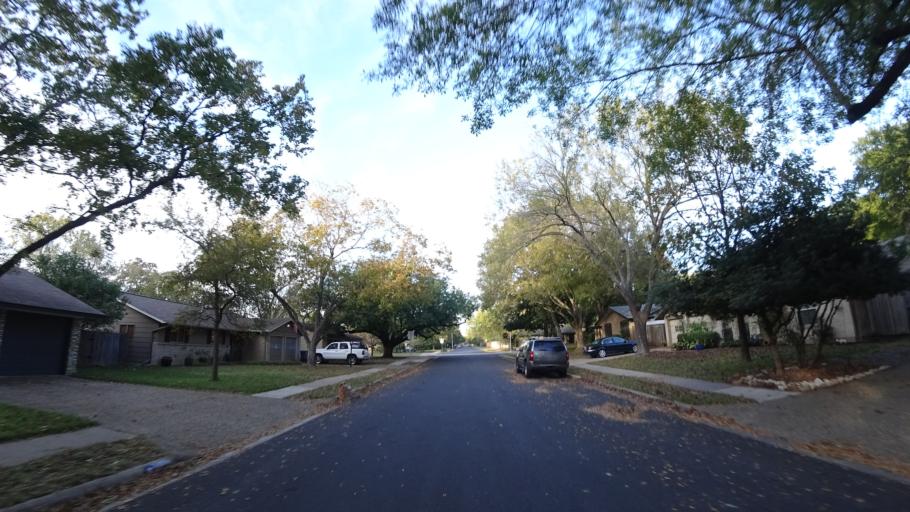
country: US
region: Texas
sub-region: Williamson County
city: Jollyville
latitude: 30.3704
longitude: -97.7364
